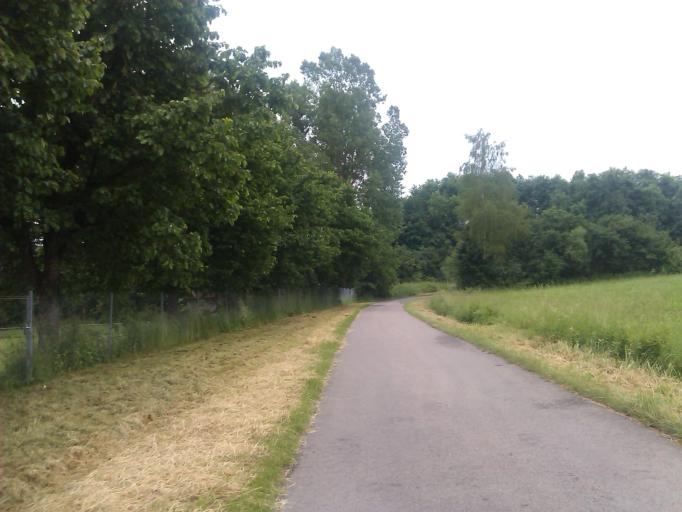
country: DE
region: Baden-Wuerttemberg
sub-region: Regierungsbezirk Stuttgart
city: Oberrot
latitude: 49.0117
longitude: 9.6665
